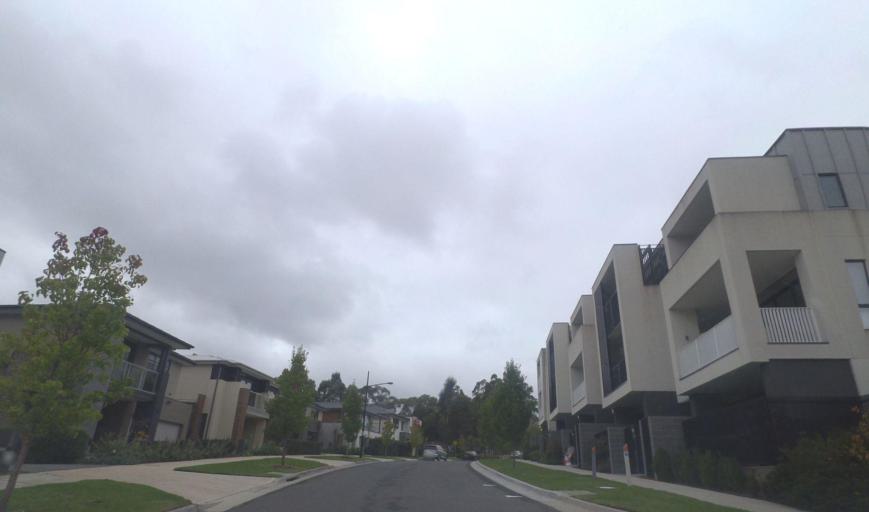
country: AU
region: Victoria
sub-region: Manningham
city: Doncaster
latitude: -37.7859
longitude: 145.1163
